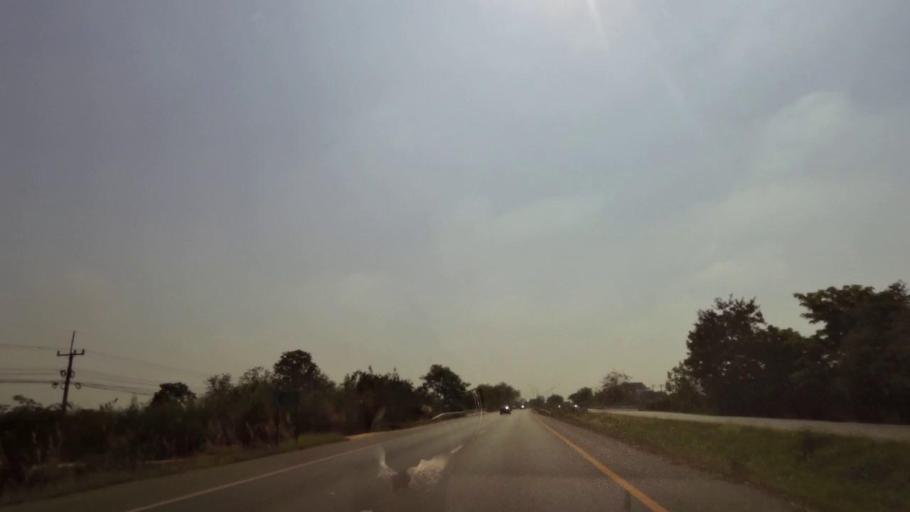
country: TH
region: Phichit
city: Wachira Barami
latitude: 16.4736
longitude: 100.1472
